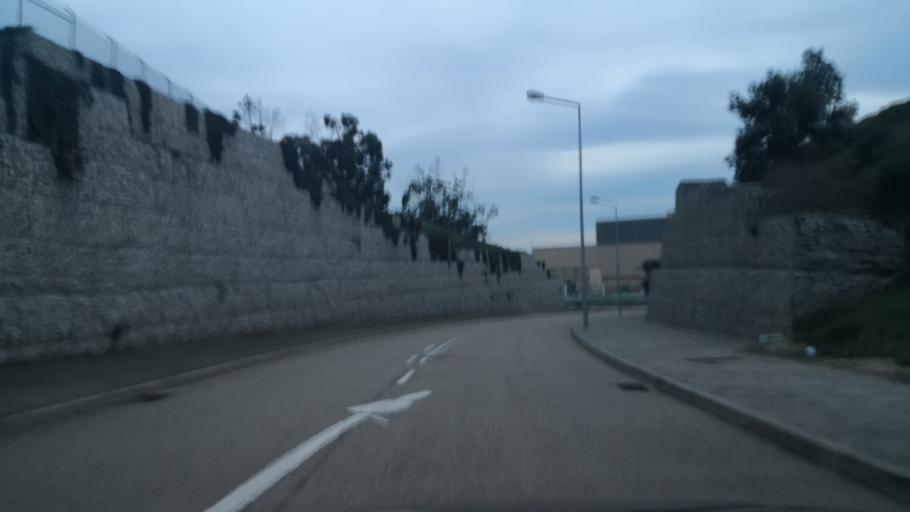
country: PT
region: Setubal
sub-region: Setubal
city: Setubal
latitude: 38.4921
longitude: -8.8182
